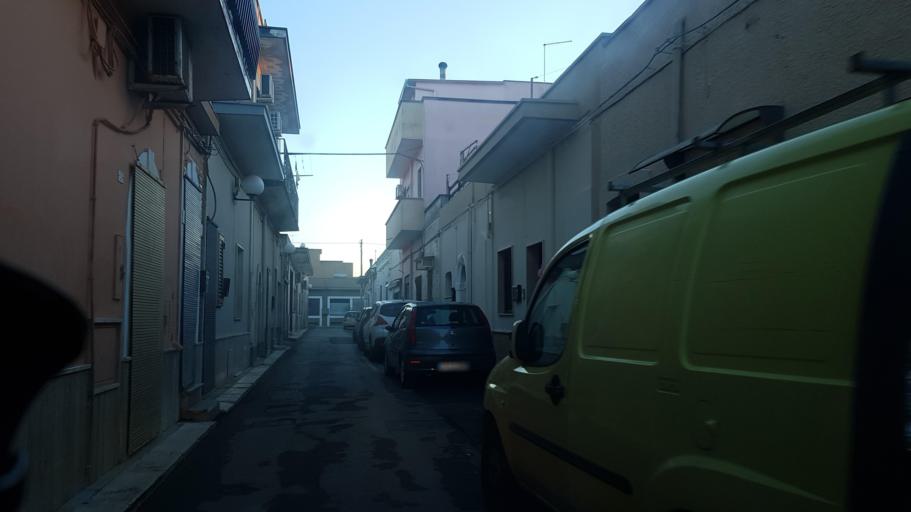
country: IT
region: Apulia
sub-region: Provincia di Brindisi
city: San Michele Salentino
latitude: 40.6299
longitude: 17.6342
